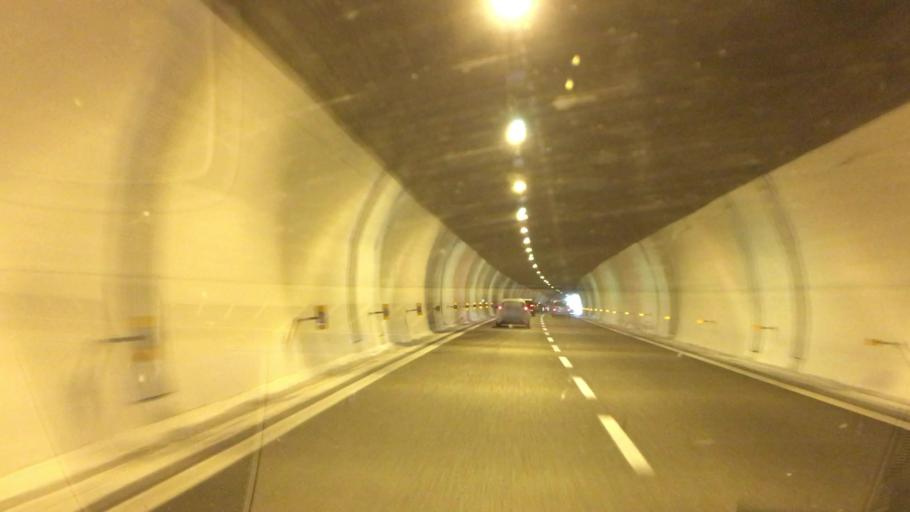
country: IT
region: Liguria
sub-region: Provincia di Genova
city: Chiavari
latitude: 44.3250
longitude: 9.3303
